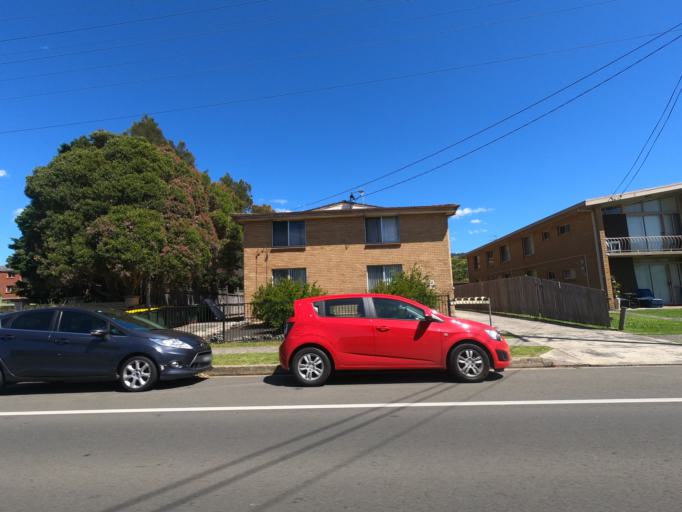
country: AU
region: New South Wales
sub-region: Wollongong
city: East Corrimal
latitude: -34.3713
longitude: 150.9097
